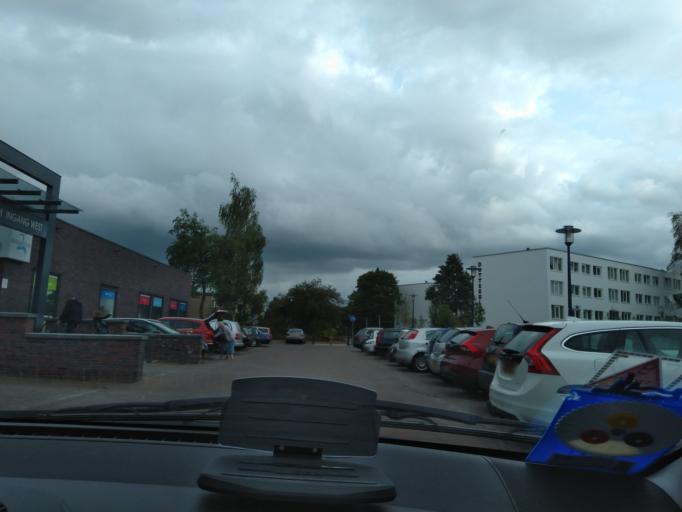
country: NL
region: Drenthe
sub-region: Gemeente Assen
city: Assen
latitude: 52.9884
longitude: 6.5802
